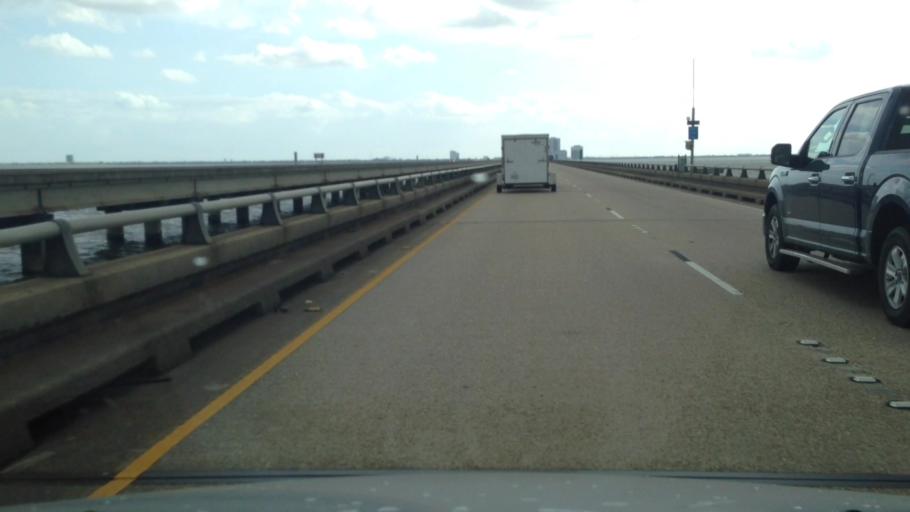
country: US
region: Louisiana
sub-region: Jefferson Parish
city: Metairie
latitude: 30.0647
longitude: -90.1466
